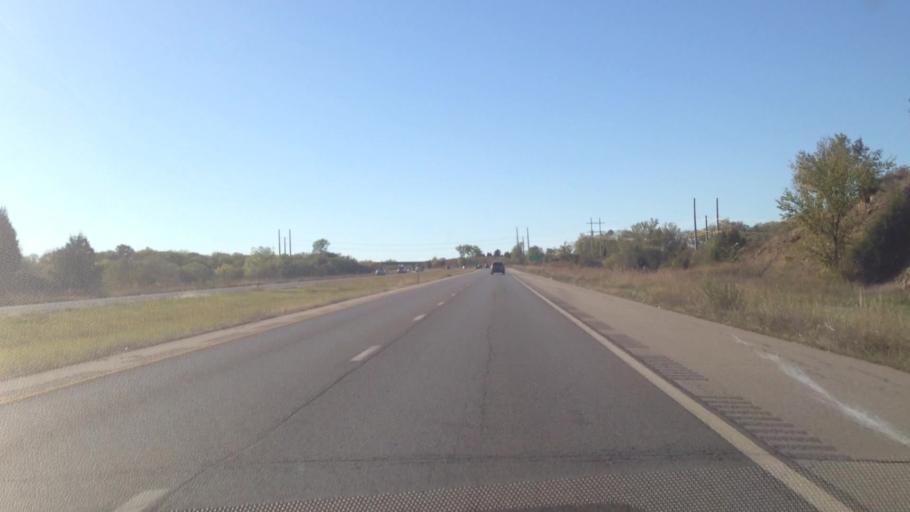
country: US
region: Kansas
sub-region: Johnson County
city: De Soto
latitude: 38.9592
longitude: -94.9273
